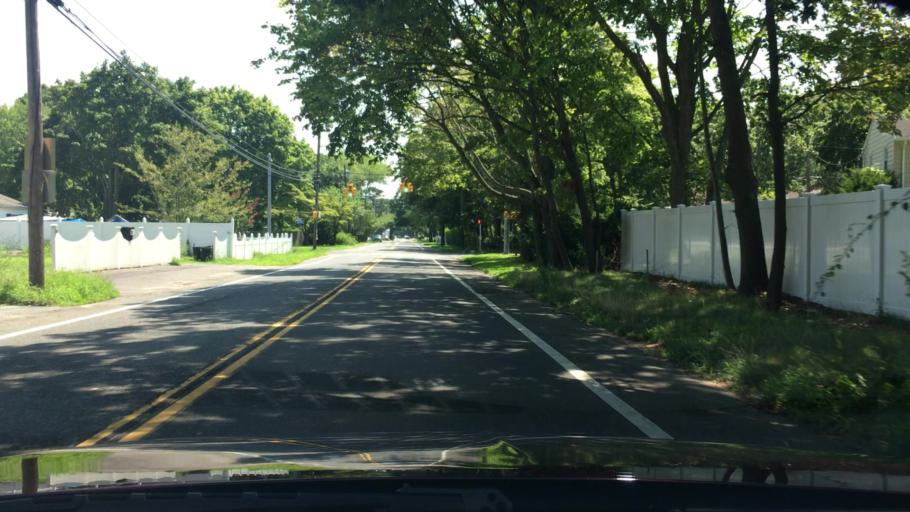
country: US
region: New York
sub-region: Suffolk County
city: Bay Wood
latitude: 40.7500
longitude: -73.2912
